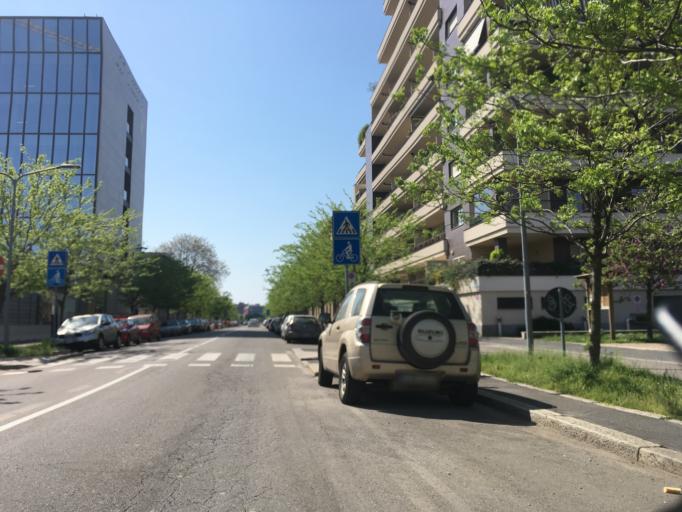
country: IT
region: Lombardy
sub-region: Citta metropolitana di Milano
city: Milano
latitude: 45.4434
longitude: 9.2031
